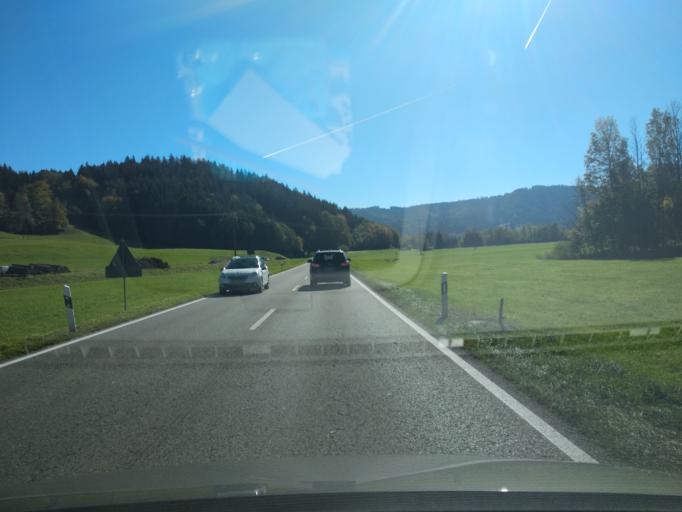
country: DE
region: Bavaria
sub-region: Swabia
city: Maierhofen
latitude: 47.6785
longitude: 10.0871
